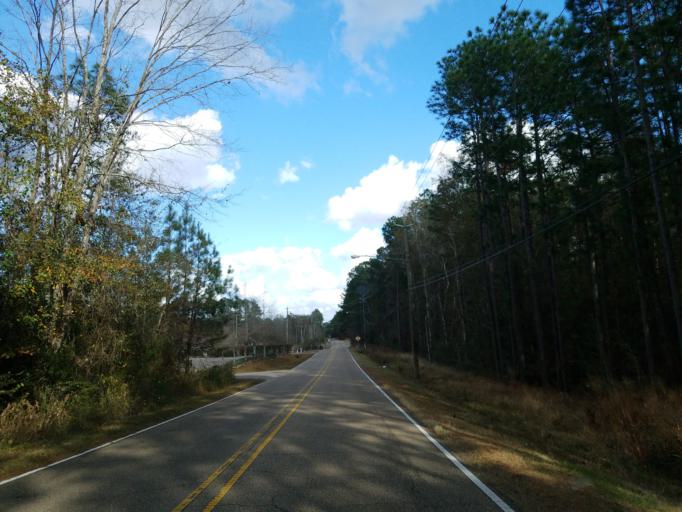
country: US
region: Mississippi
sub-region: Lamar County
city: West Hattiesburg
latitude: 31.2904
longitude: -89.3300
